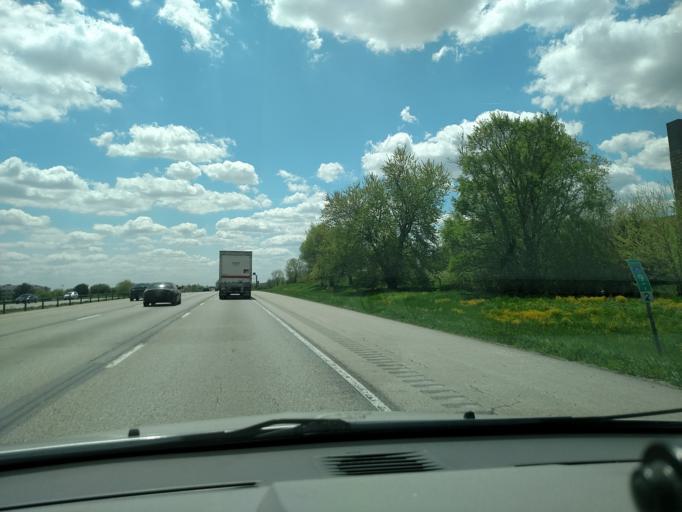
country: US
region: Iowa
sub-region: Polk County
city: Ankeny
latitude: 41.7109
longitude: -93.5765
